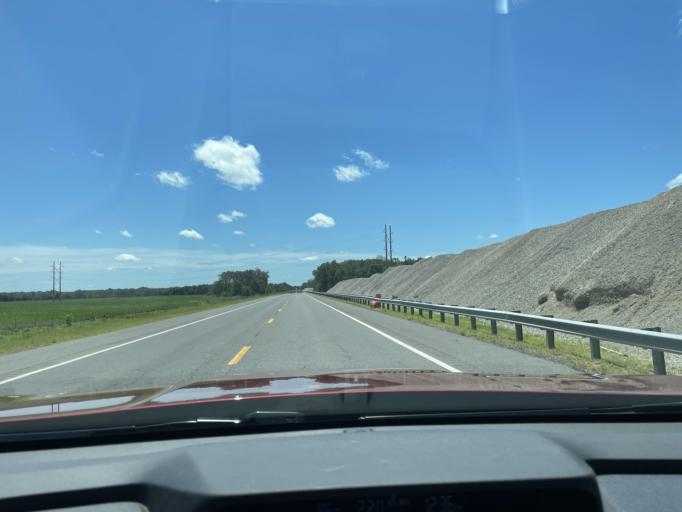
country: US
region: Arkansas
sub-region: Jefferson County
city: Pine Bluff
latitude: 34.1543
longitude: -91.9804
